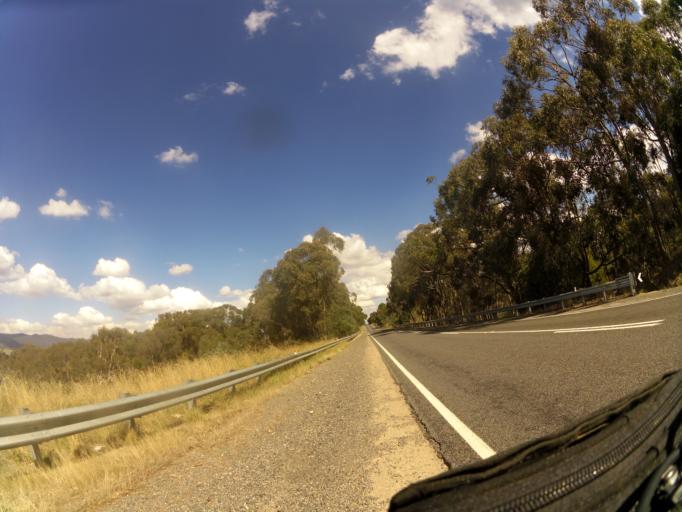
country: AU
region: Victoria
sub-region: Mansfield
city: Mansfield
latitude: -36.8823
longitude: 145.9944
